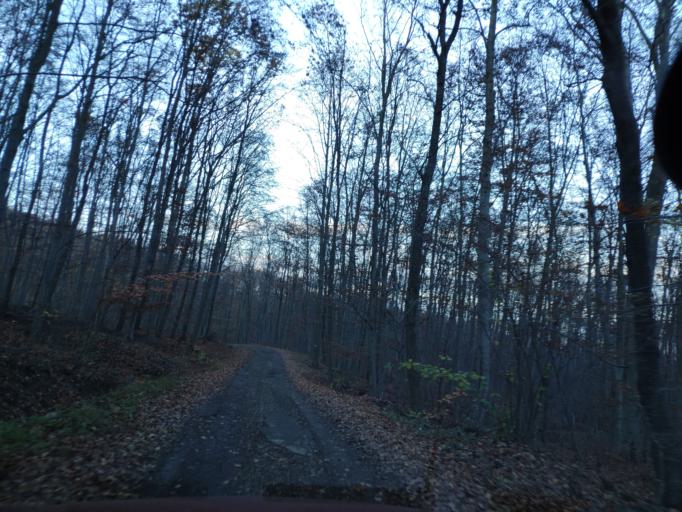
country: SK
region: Kosicky
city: Secovce
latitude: 48.5870
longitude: 21.5059
